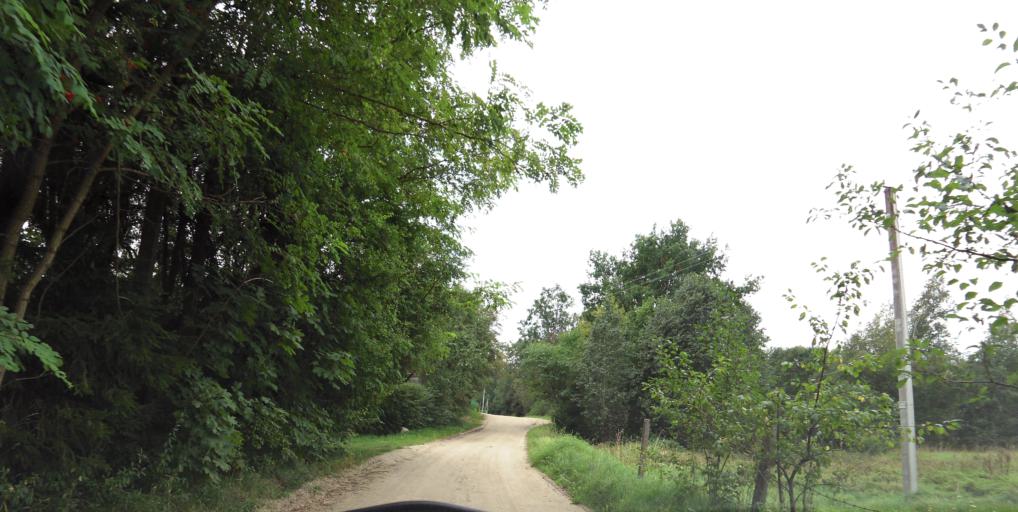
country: LT
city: Grigiskes
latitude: 54.7621
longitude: 25.0221
